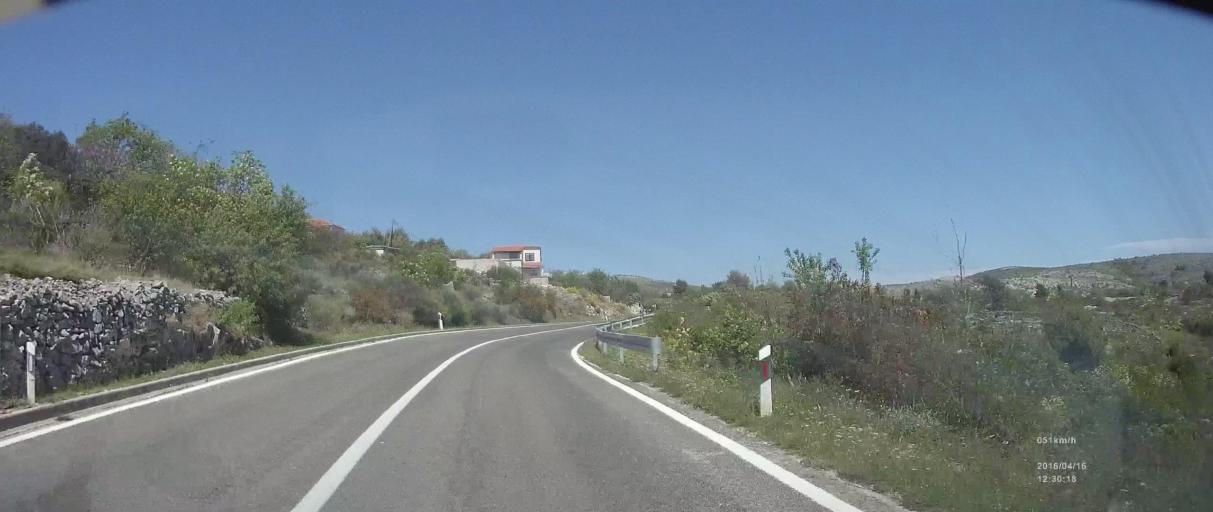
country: HR
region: Splitsko-Dalmatinska
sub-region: Grad Trogir
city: Trogir
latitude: 43.5291
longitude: 16.2179
